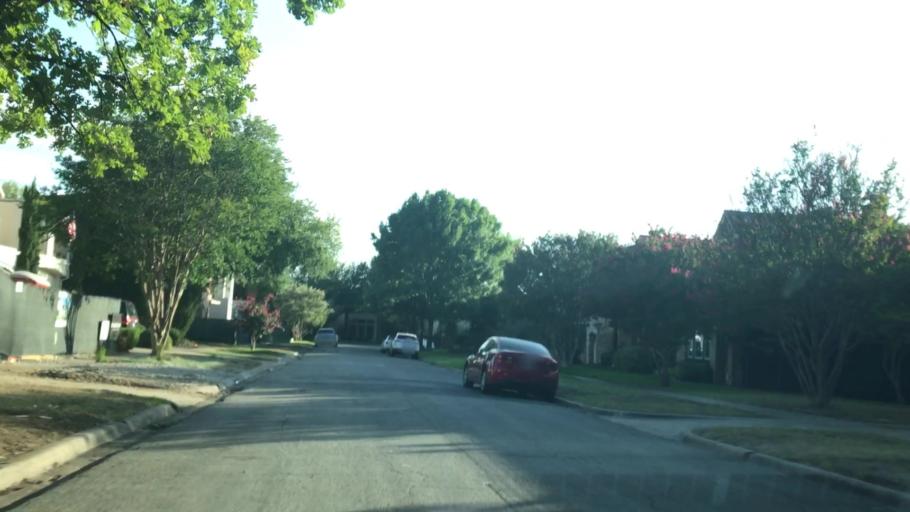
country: US
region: Texas
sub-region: Dallas County
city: University Park
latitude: 32.8311
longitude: -96.8225
